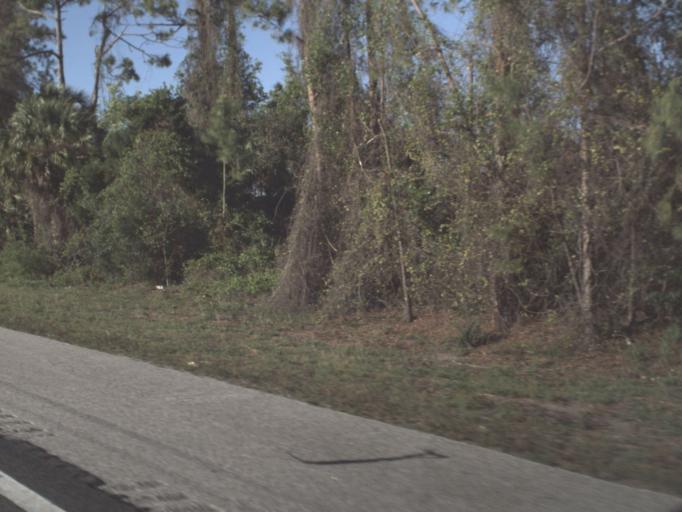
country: US
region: Florida
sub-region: Flagler County
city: Flagler Beach
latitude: 29.4240
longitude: -81.1638
